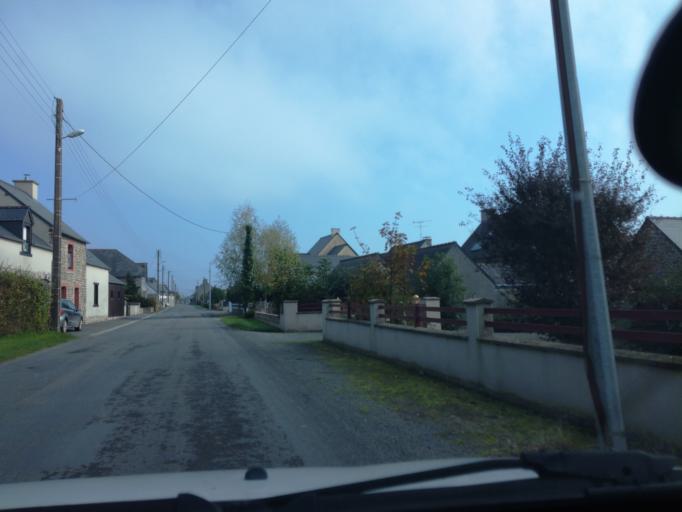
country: FR
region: Brittany
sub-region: Departement d'Ille-et-Vilaine
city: Cherrueix
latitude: 48.6064
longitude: -1.7064
